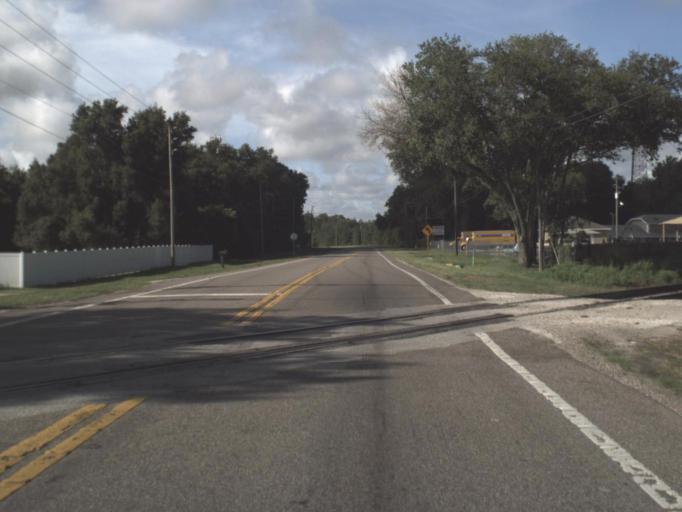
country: US
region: Florida
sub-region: Pasco County
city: Shady Hills
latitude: 28.3567
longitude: -82.5040
